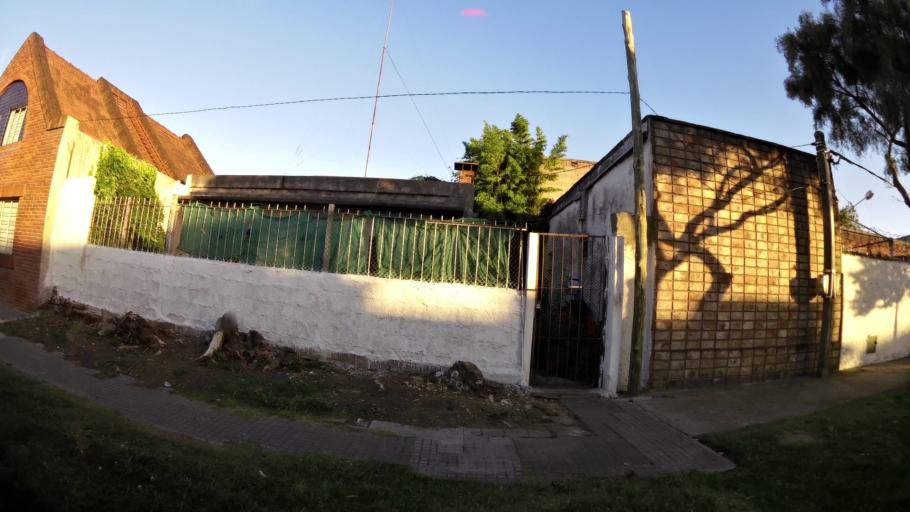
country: UY
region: Montevideo
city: Montevideo
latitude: -34.8381
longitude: -56.1499
